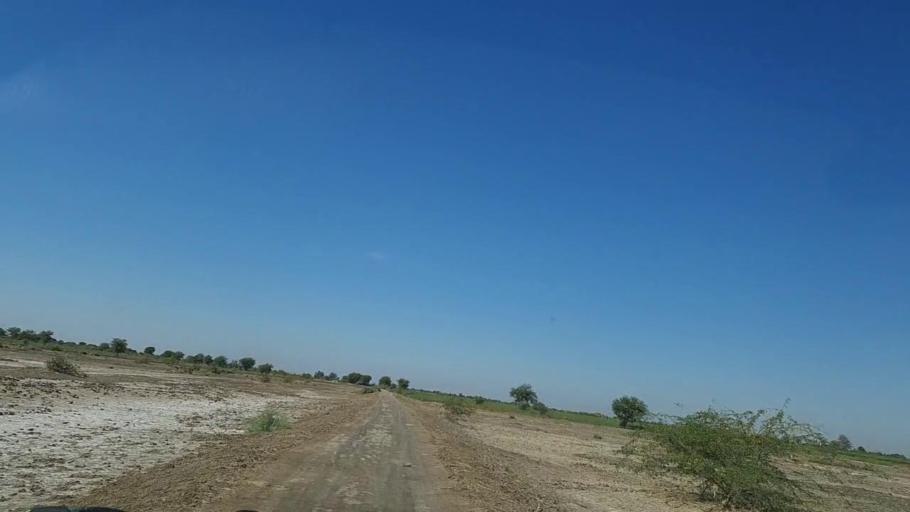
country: PK
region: Sindh
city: Pithoro
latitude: 25.5580
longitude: 69.4605
